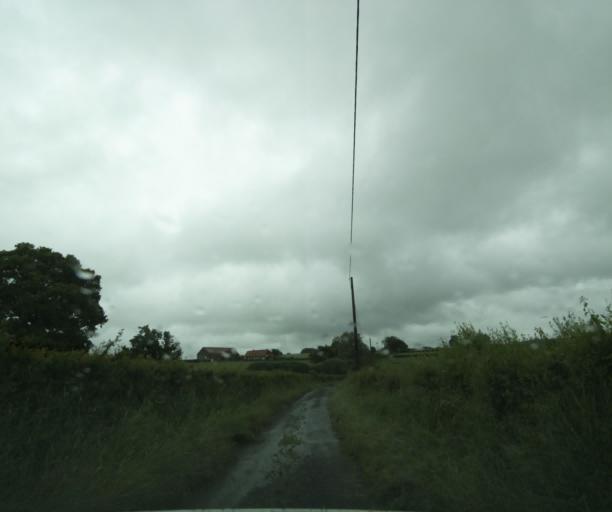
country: FR
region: Bourgogne
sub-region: Departement de Saone-et-Loire
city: Ciry-le-Noble
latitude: 46.5189
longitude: 4.3832
